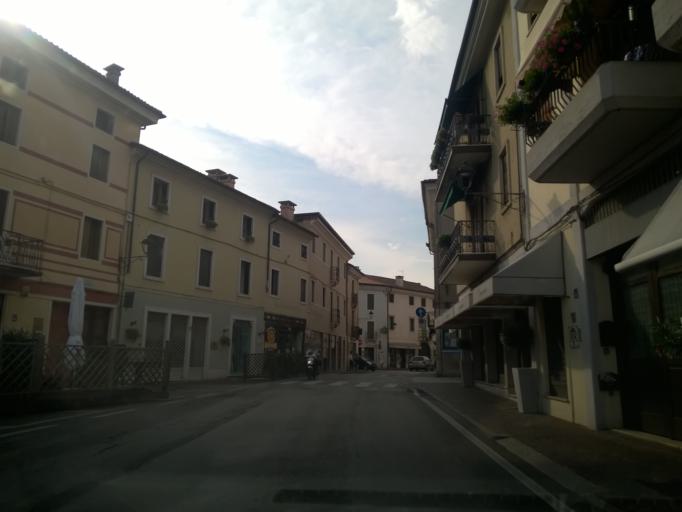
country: IT
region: Veneto
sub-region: Provincia di Vicenza
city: Malo
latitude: 45.6564
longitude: 11.4061
